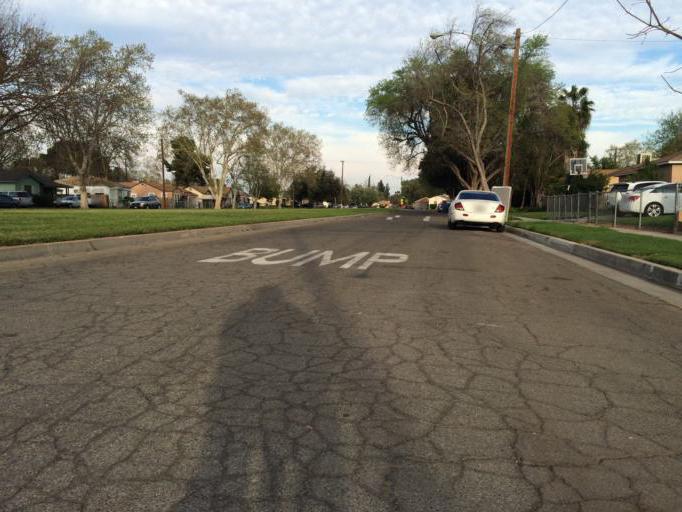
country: US
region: California
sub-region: Fresno County
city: Fresno
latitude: 36.7467
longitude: -119.7449
